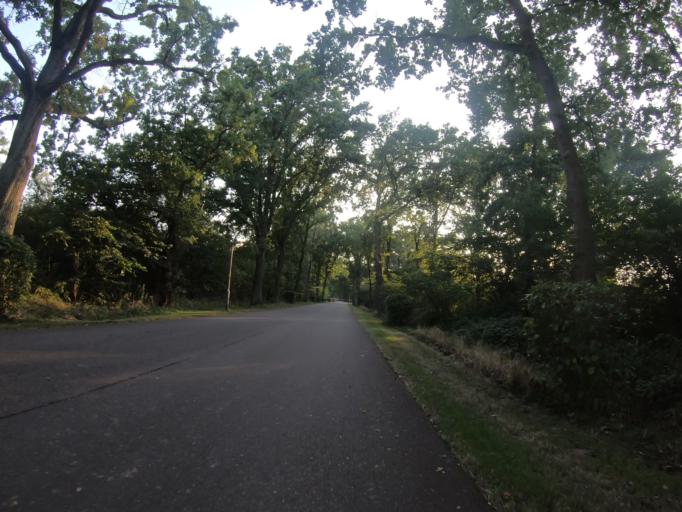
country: DE
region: Lower Saxony
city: Calberlah
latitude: 52.4505
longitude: 10.6149
